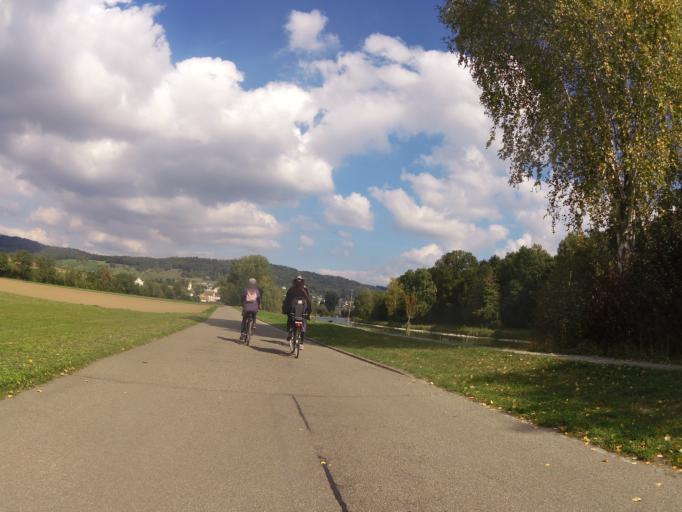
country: CH
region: Zurich
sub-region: Bezirk Dietikon
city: Schlieren / Spital
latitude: 47.4023
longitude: 8.4330
